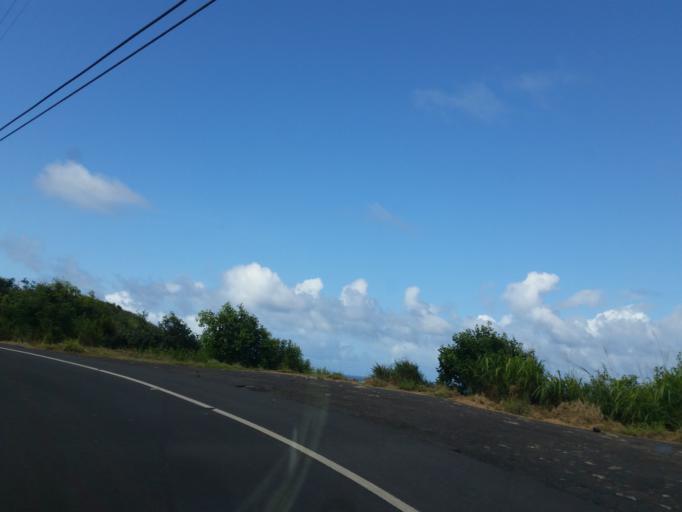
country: US
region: Hawaii
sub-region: Maui County
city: Waihee-Waiehu
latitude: 20.9497
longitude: -156.5178
